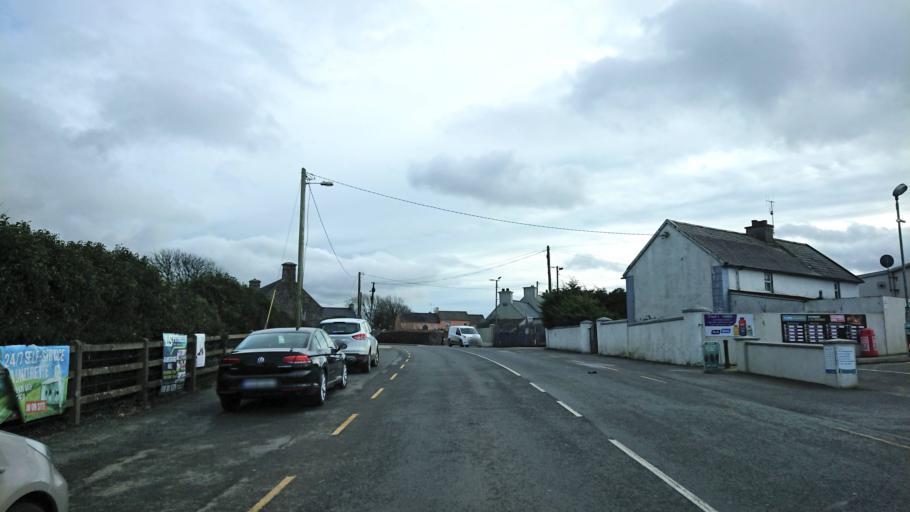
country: IE
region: Munster
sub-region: Waterford
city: Dunmore East
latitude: 52.2455
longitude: -6.9219
